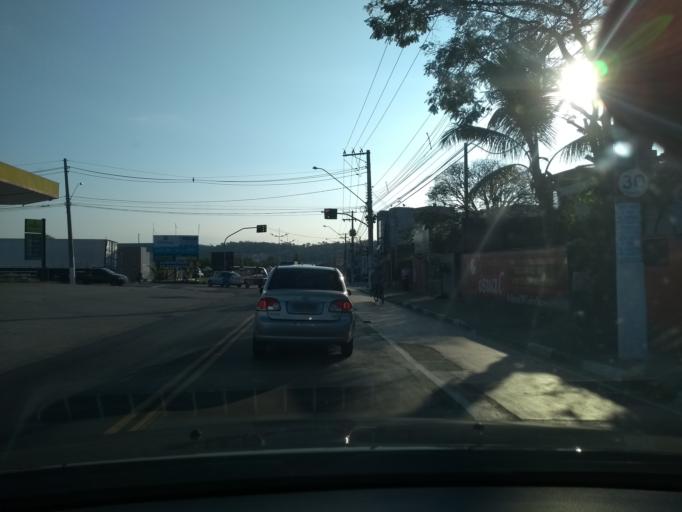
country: BR
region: Sao Paulo
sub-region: Itupeva
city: Itupeva
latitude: -23.1513
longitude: -47.0493
